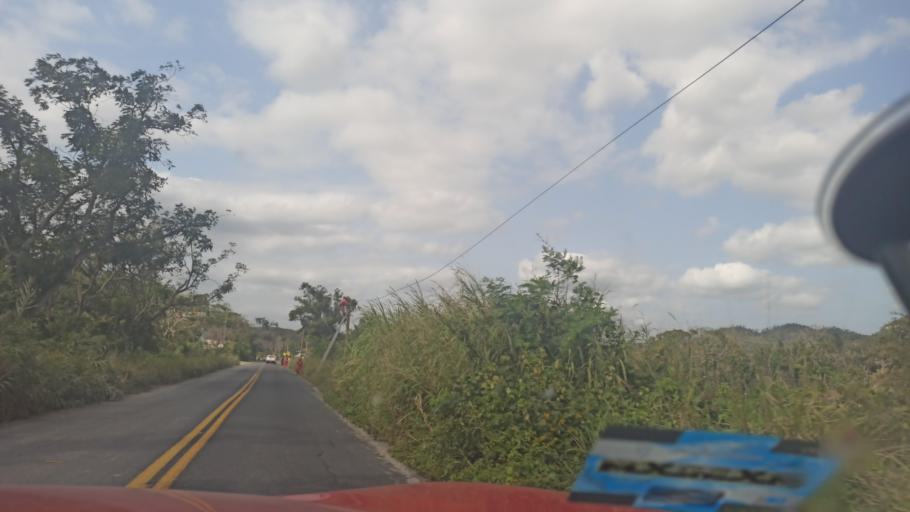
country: MX
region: Veracruz
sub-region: Papantla
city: Polutla
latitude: 20.4636
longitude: -97.2540
